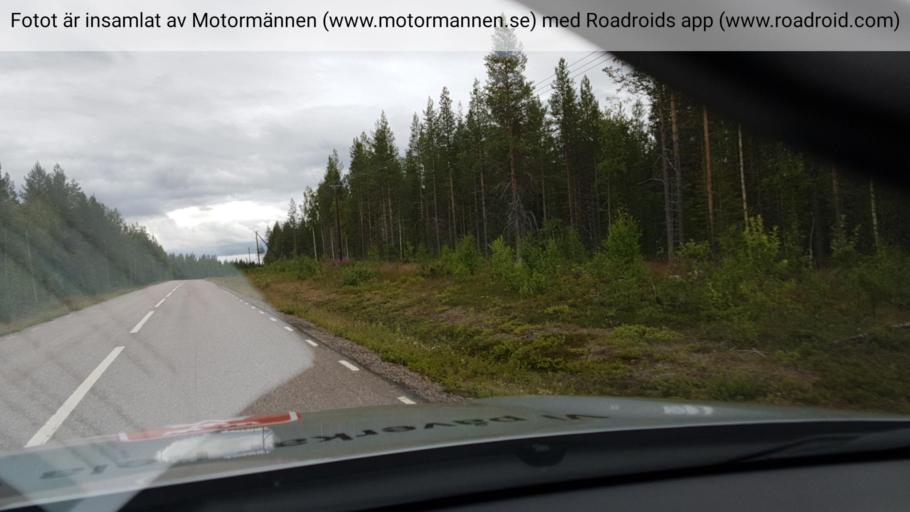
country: SE
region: Norrbotten
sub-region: Overkalix Kommun
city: OEverkalix
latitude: 66.7638
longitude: 22.9033
